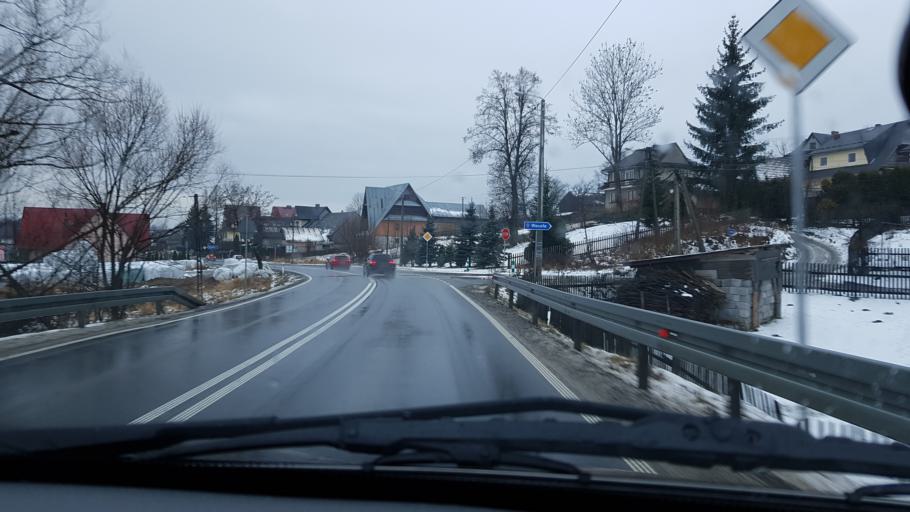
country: PL
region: Lesser Poland Voivodeship
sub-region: Powiat nowotarski
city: Sieniawa
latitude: 49.5067
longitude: 19.8895
